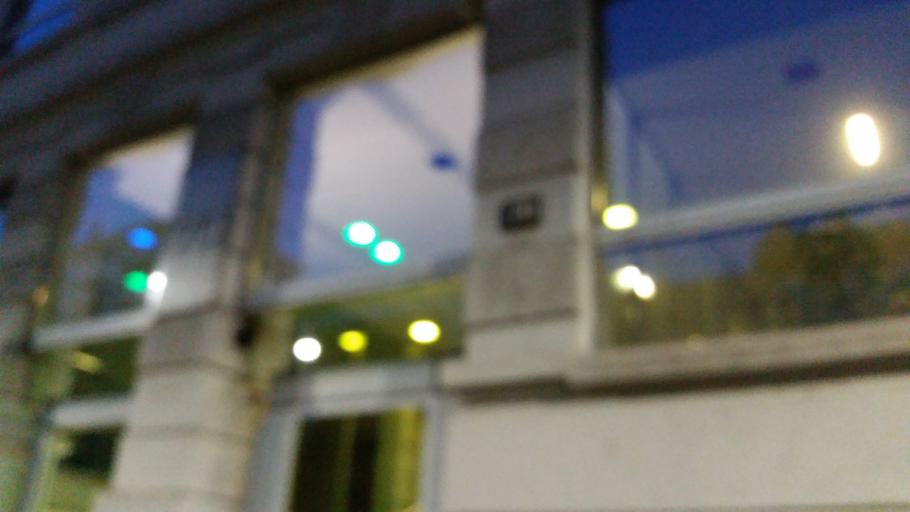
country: IT
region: Lombardy
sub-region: Citta metropolitana di Milano
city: Milano
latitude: 45.4603
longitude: 9.1547
